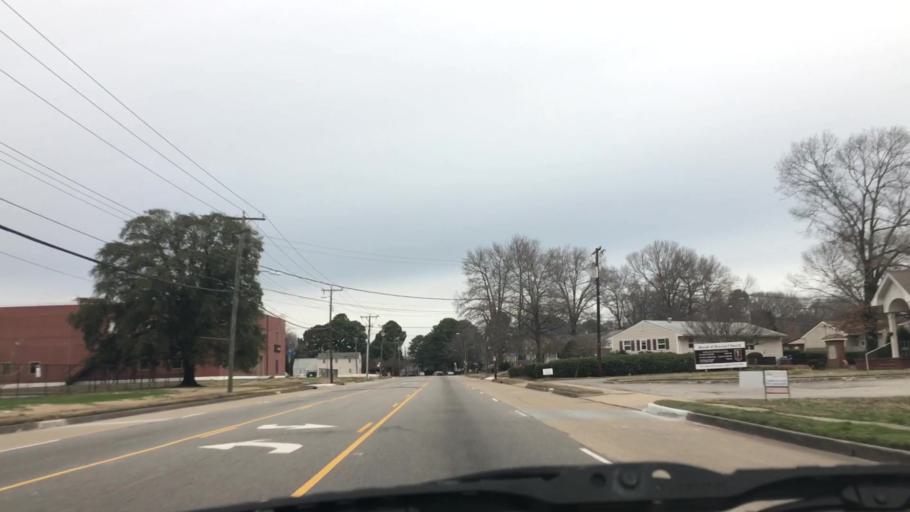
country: US
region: Virginia
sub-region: City of Norfolk
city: Norfolk
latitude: 36.8796
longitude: -76.2335
